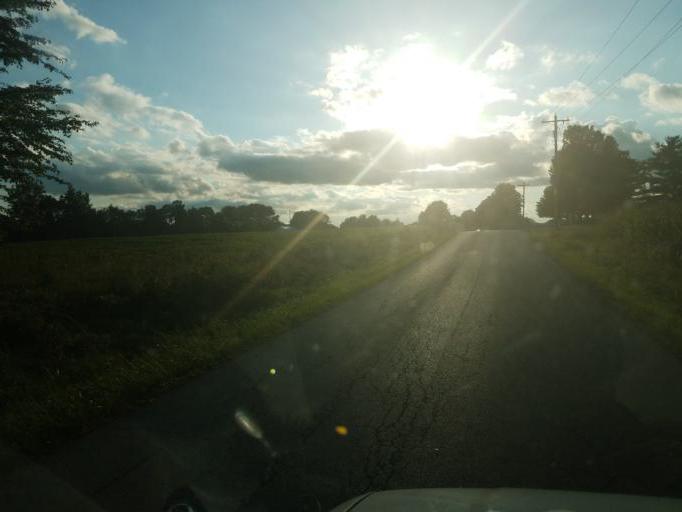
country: US
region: Ohio
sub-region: Knox County
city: Centerburg
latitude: 40.4338
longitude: -82.6967
